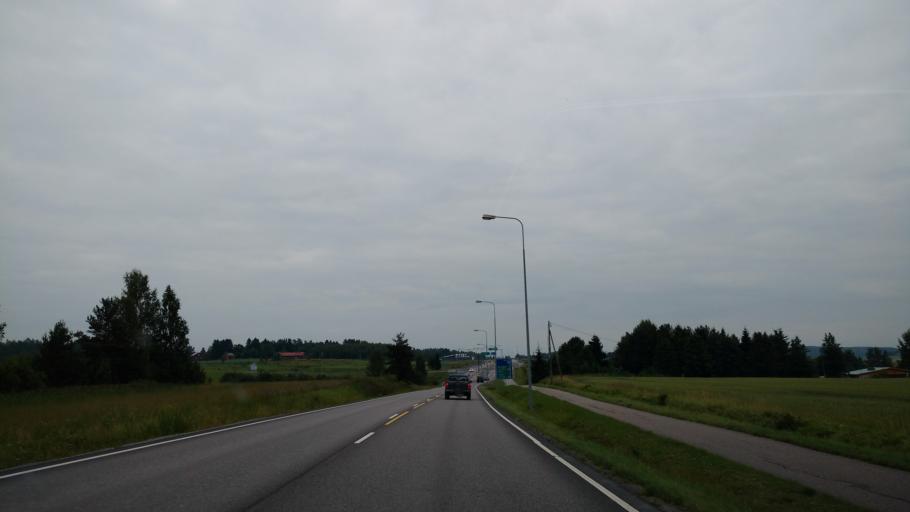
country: FI
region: Varsinais-Suomi
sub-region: Salo
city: Halikko
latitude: 60.4311
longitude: 23.0479
